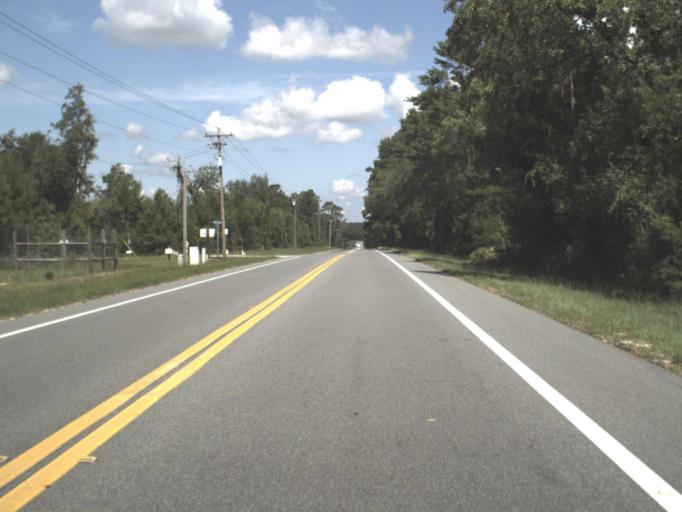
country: US
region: Florida
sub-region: Putnam County
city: Interlachen
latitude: 29.7291
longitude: -81.8540
